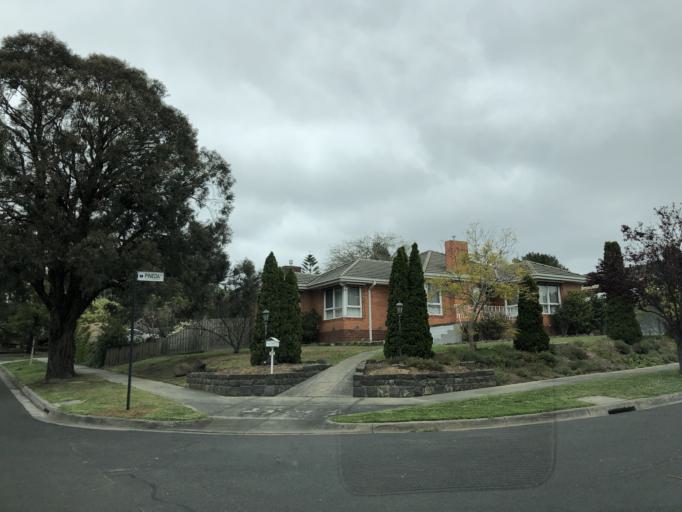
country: AU
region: Victoria
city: Burwood East
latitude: -37.8632
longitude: 145.1641
